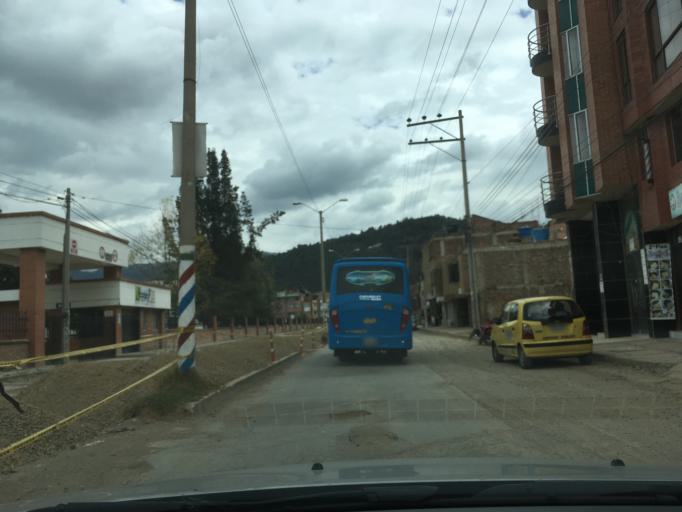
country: CO
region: Boyaca
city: Sogamoso
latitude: 5.7040
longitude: -72.9422
